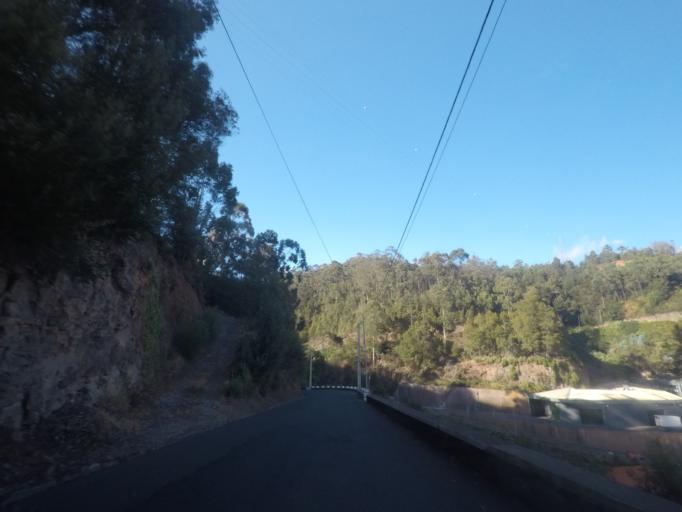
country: PT
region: Madeira
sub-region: Ribeira Brava
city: Campanario
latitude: 32.6673
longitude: -17.0010
